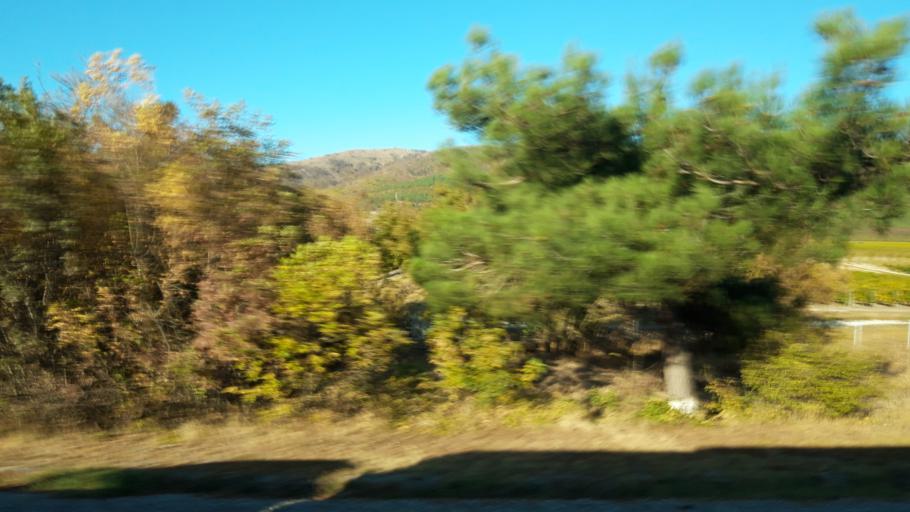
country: RU
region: Krasnodarskiy
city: Kabardinka
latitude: 44.6258
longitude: 38.0082
